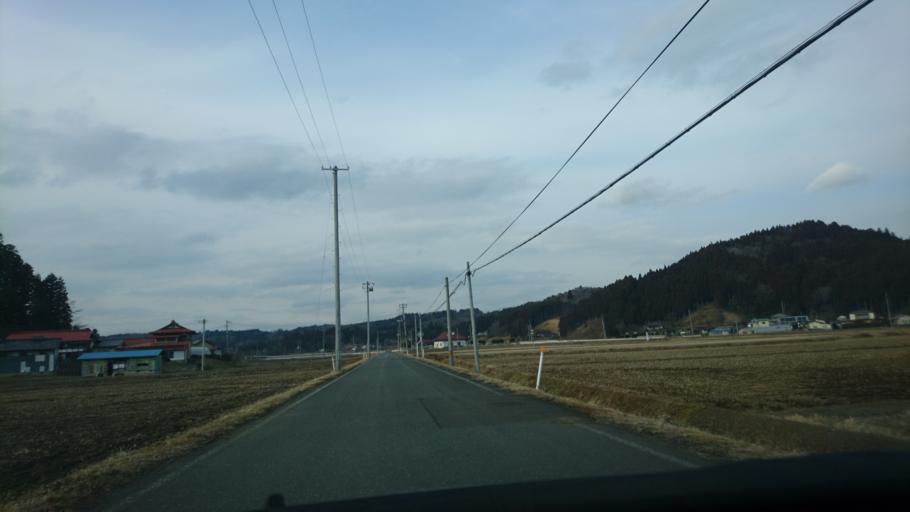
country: JP
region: Iwate
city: Ichinoseki
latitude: 38.8314
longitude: 141.2471
